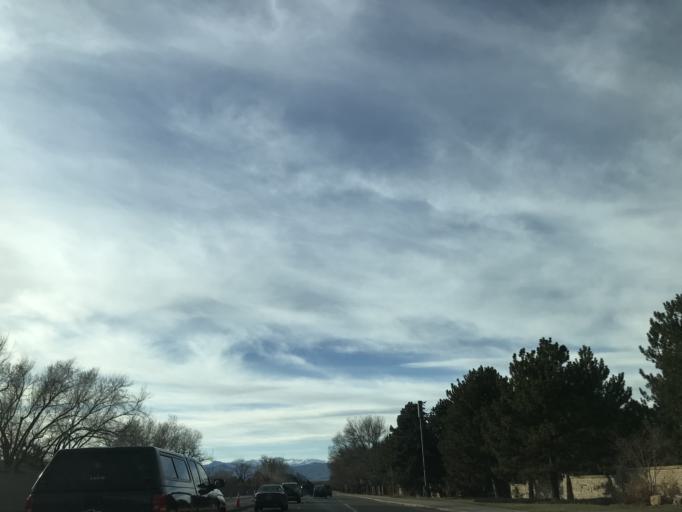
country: US
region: Colorado
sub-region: Arapahoe County
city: Greenwood Village
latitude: 39.6243
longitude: -104.9502
